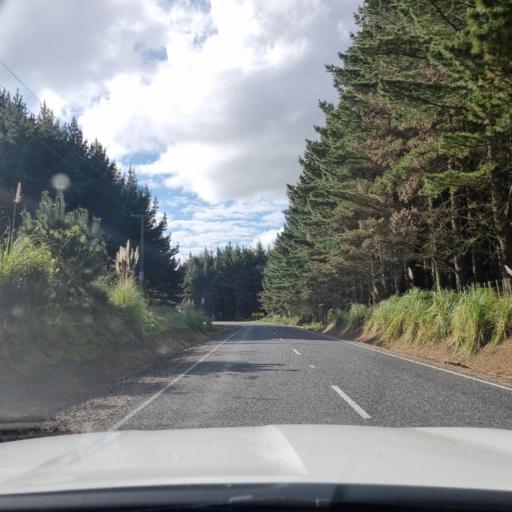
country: NZ
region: Northland
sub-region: Kaipara District
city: Dargaville
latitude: -36.2380
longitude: 174.0468
